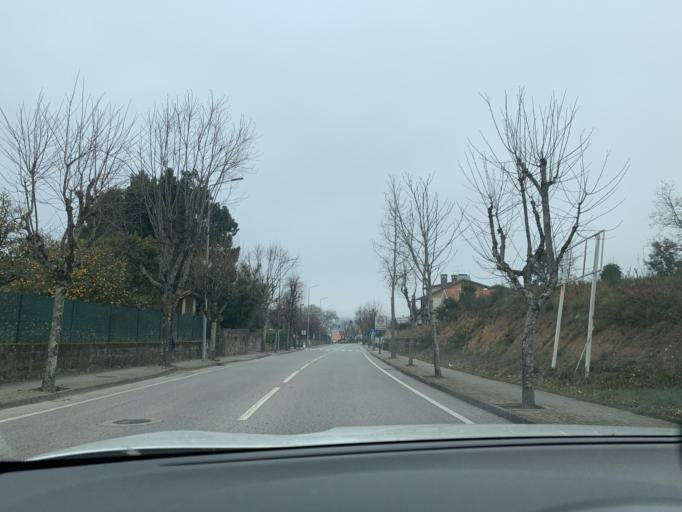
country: PT
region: Viseu
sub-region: Concelho de Tondela
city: Tondela
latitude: 40.5082
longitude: -8.0805
